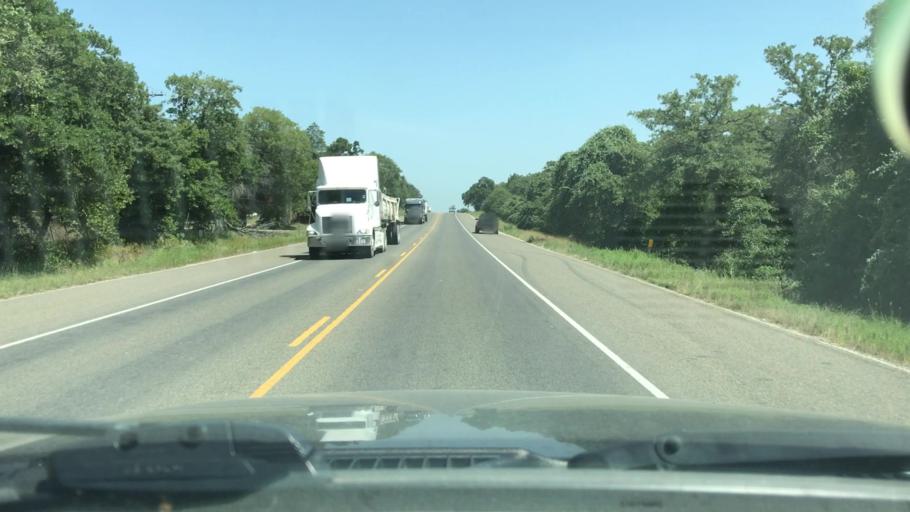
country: US
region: Texas
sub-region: Bastrop County
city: Elgin
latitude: 30.3023
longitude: -97.3475
